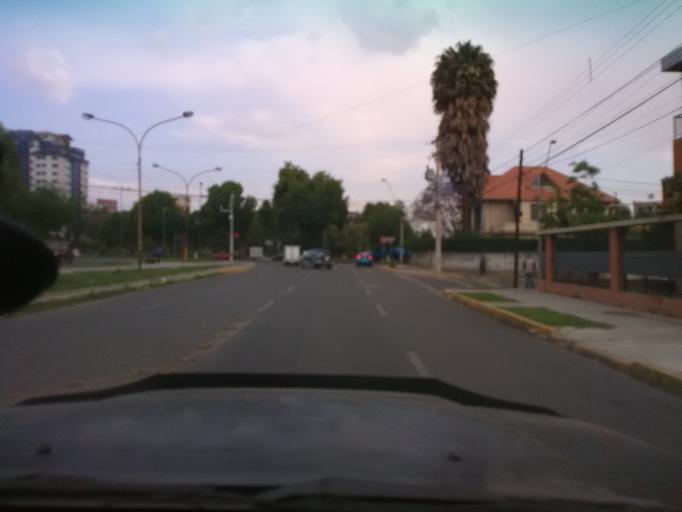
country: BO
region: Cochabamba
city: Cochabamba
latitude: -17.3815
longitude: -66.1627
